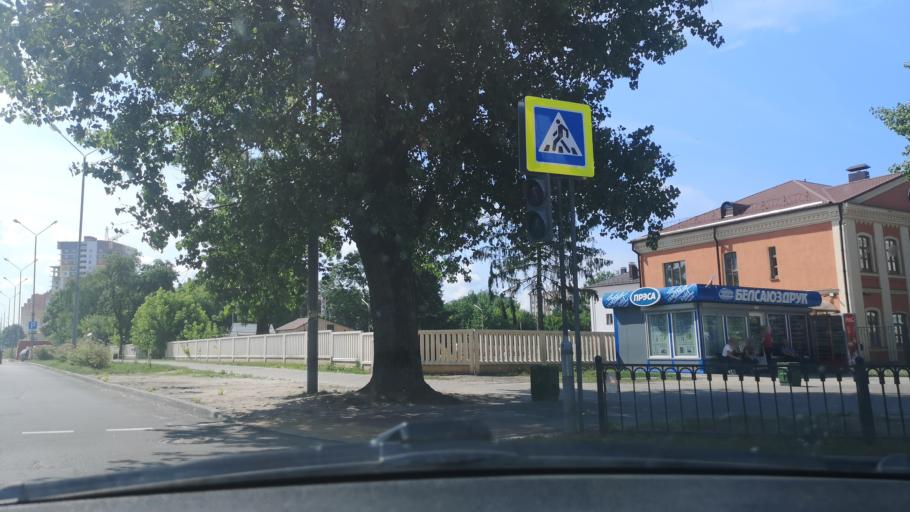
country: BY
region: Brest
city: Brest
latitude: 52.0997
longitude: 23.7008
